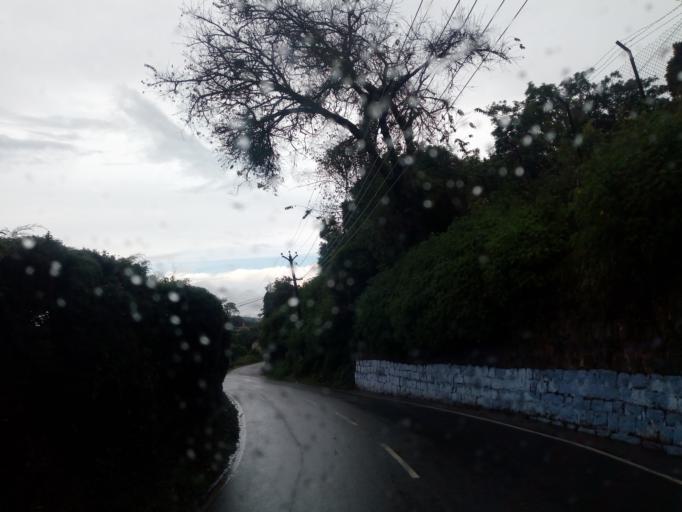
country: IN
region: Tamil Nadu
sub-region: Nilgiri
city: Wellington
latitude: 11.3457
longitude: 76.8017
